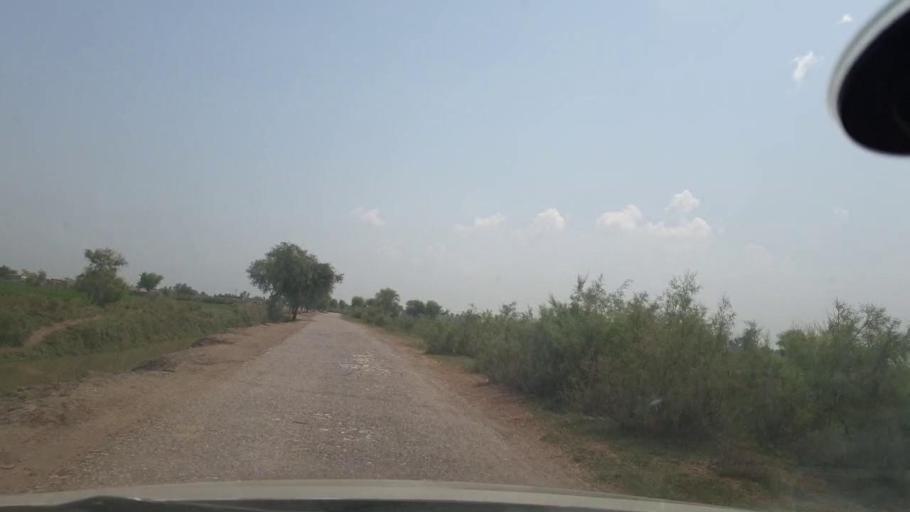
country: PK
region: Sindh
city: Jacobabad
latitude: 28.1310
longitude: 68.3800
